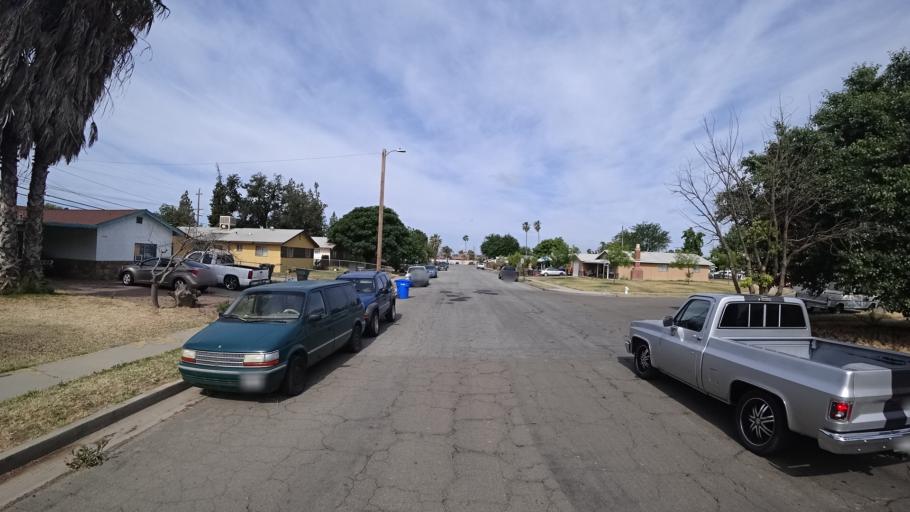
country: US
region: California
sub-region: Kings County
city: Hanford
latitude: 36.3139
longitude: -119.6685
